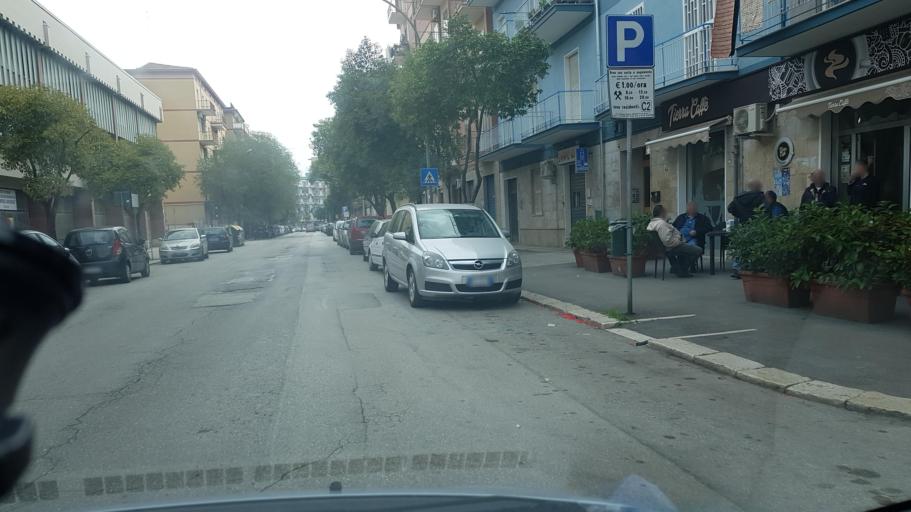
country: IT
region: Apulia
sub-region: Provincia di Foggia
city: Foggia
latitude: 41.4552
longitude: 15.5562
